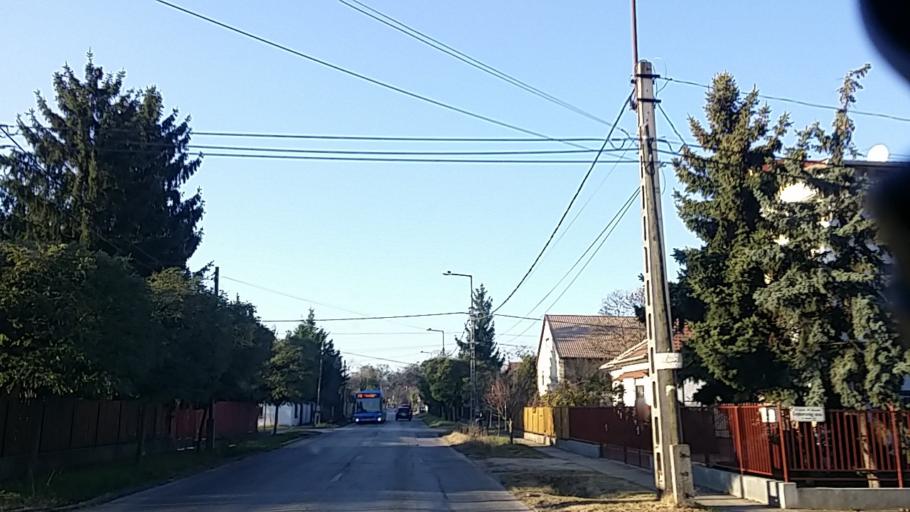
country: HU
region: Budapest
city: Budapest XVI. keruelet
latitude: 47.5066
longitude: 19.2109
